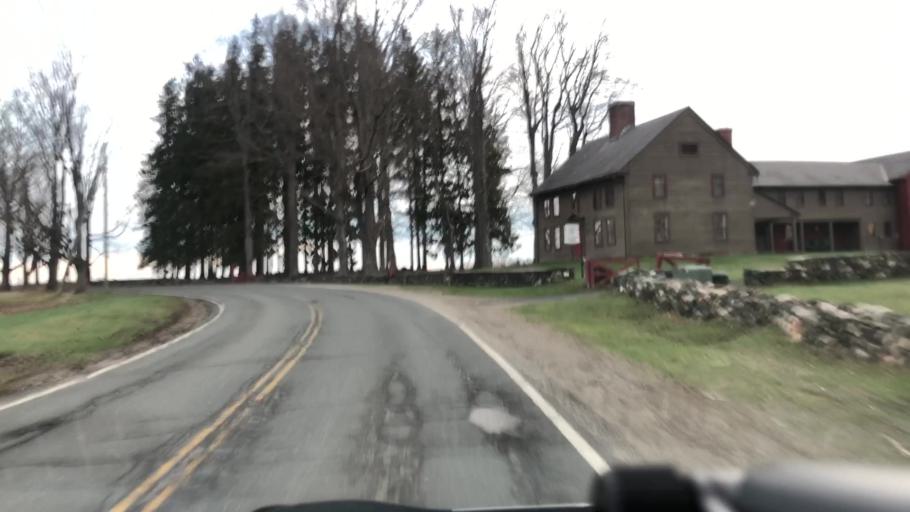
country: US
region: Massachusetts
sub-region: Hampshire County
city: Chesterfield
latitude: 42.4121
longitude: -72.9364
